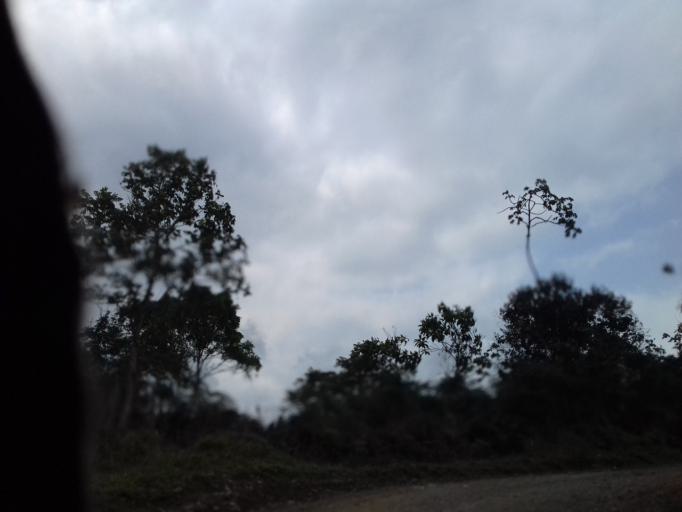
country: CO
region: Tolima
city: Libano
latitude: 4.9365
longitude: -75.0692
